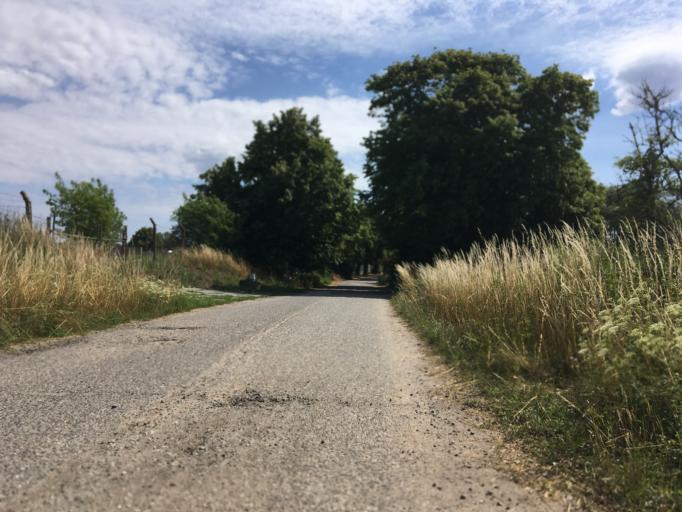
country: DE
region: Brandenburg
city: Casekow
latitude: 53.2038
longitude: 14.1479
